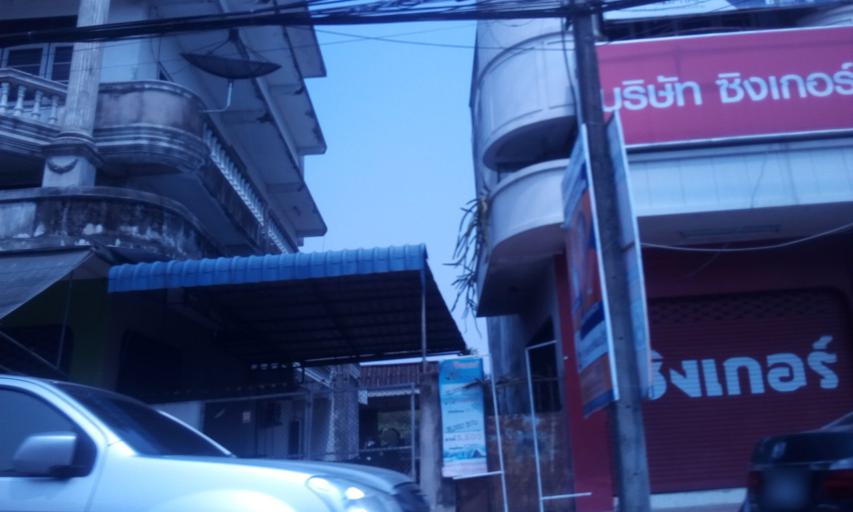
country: TH
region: Chon Buri
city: Phanat Nikhom
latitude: 13.4466
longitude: 101.1769
